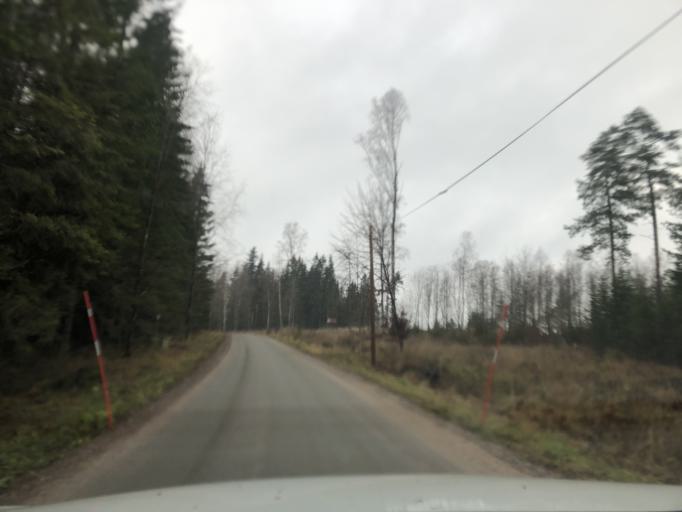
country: SE
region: Vaestra Goetaland
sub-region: Ulricehamns Kommun
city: Ulricehamn
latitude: 57.8587
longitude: 13.6168
